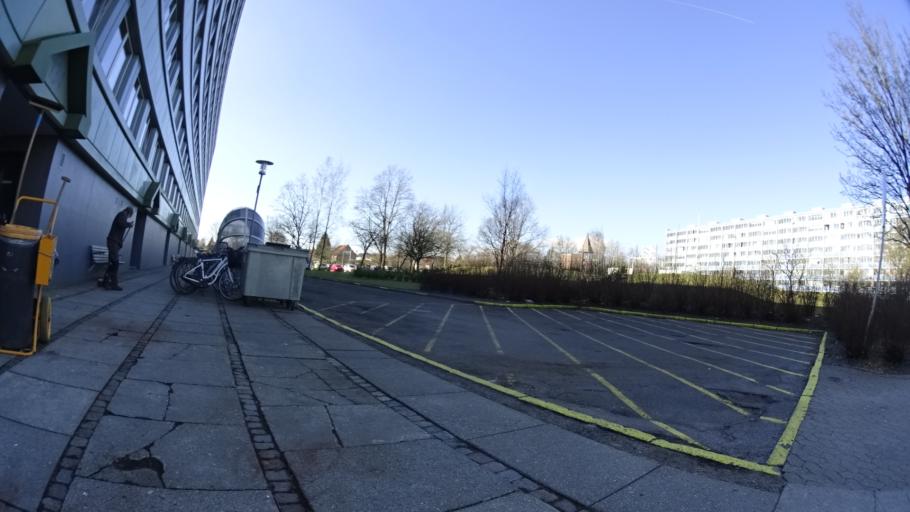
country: DK
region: Central Jutland
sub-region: Arhus Kommune
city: Arhus
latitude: 56.1704
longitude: 10.1740
